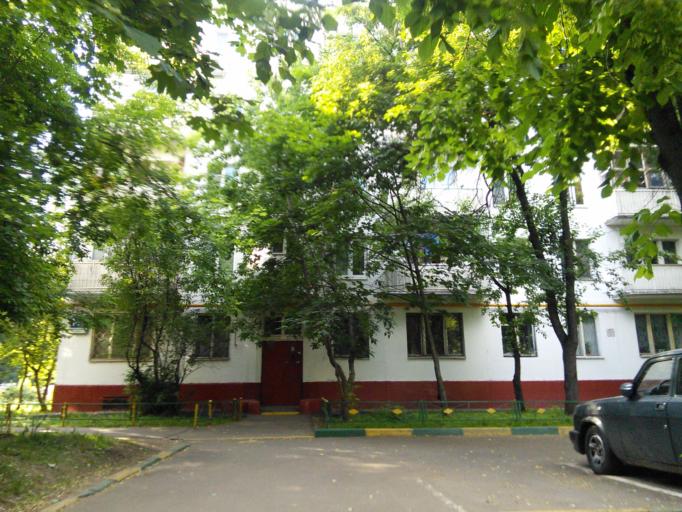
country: RU
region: Moskovskaya
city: Bogorodskoye
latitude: 55.8103
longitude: 37.7236
